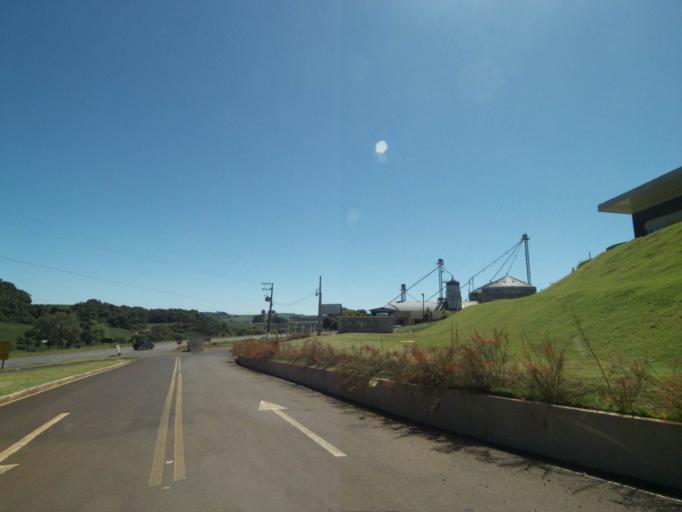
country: BR
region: Parana
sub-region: Pato Branco
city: Pato Branco
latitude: -26.2574
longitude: -52.7857
